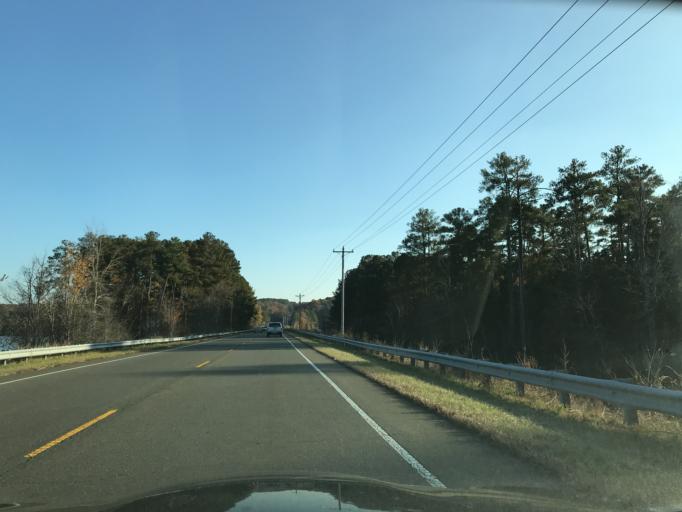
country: US
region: North Carolina
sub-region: Granville County
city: Creedmoor
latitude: 36.0203
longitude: -78.6935
